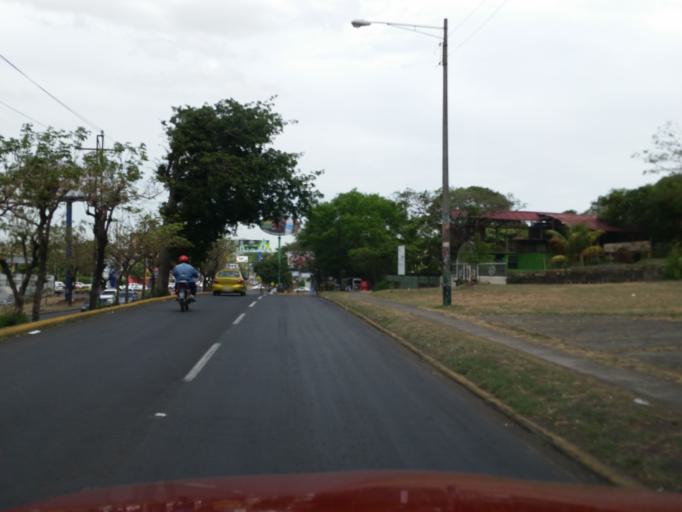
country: NI
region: Managua
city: Managua
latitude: 12.1367
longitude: -86.2737
